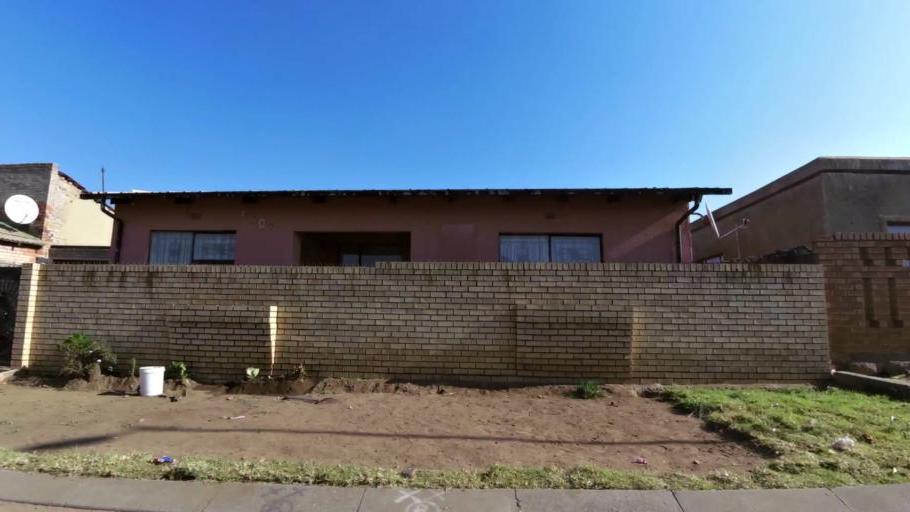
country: ZA
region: Gauteng
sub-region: City of Johannesburg Metropolitan Municipality
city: Soweto
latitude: -26.2478
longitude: 27.9294
